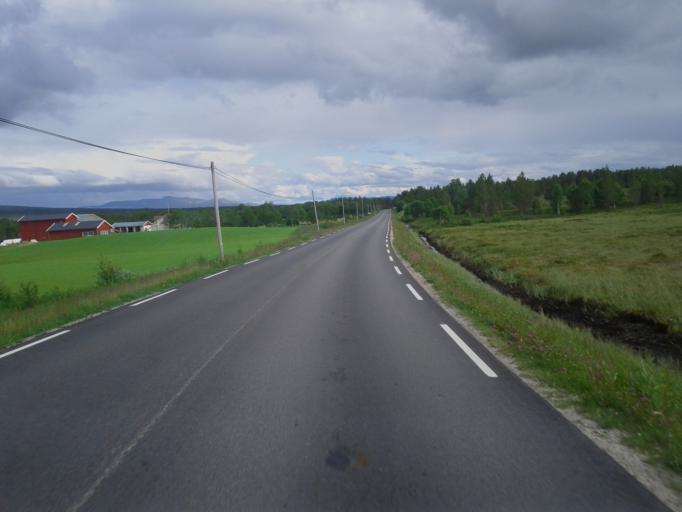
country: NO
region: Sor-Trondelag
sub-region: Roros
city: Roros
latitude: 62.3023
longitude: 11.7195
